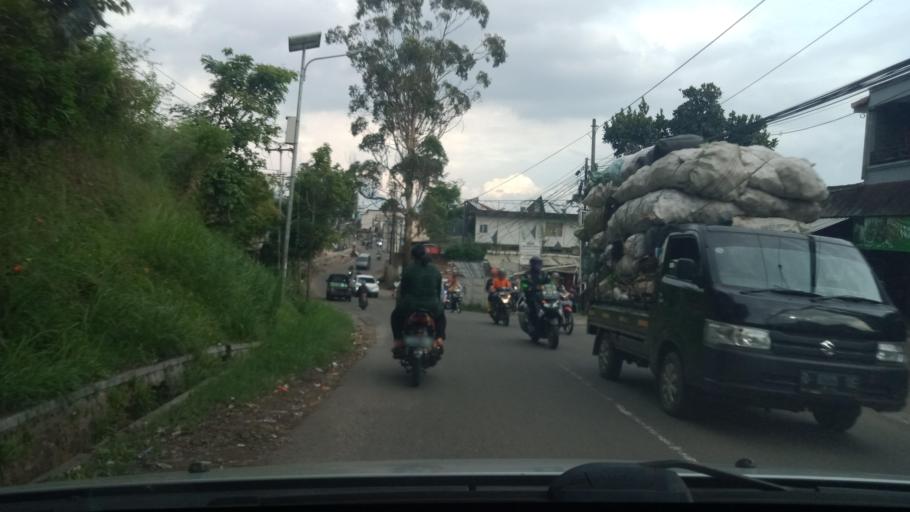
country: ID
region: West Java
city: Lembang
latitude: -6.8038
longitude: 107.5849
